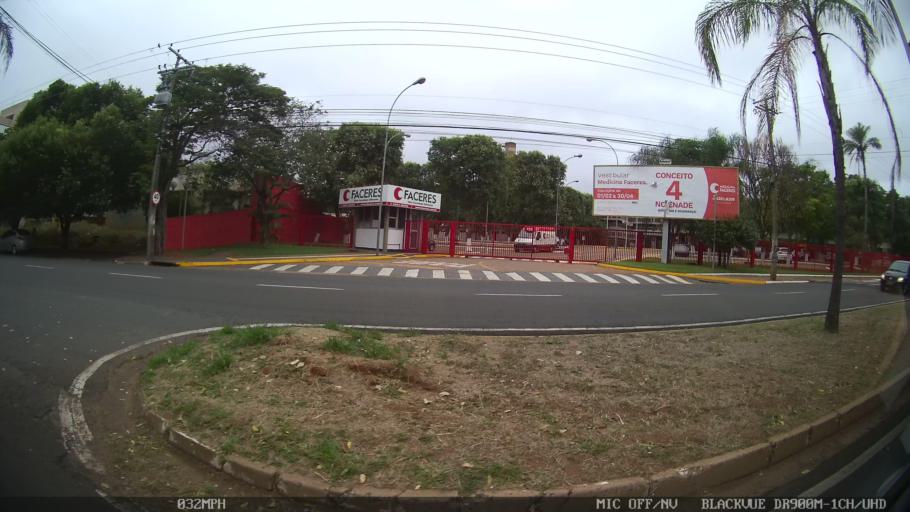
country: BR
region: Sao Paulo
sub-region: Sao Jose Do Rio Preto
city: Sao Jose do Rio Preto
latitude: -20.8380
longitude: -49.4010
